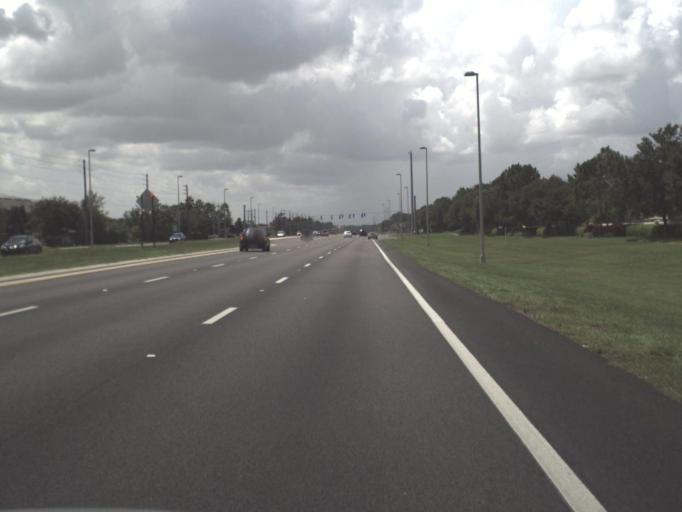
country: US
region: Florida
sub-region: Hillsborough County
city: Riverview
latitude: 27.8153
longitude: -82.3324
